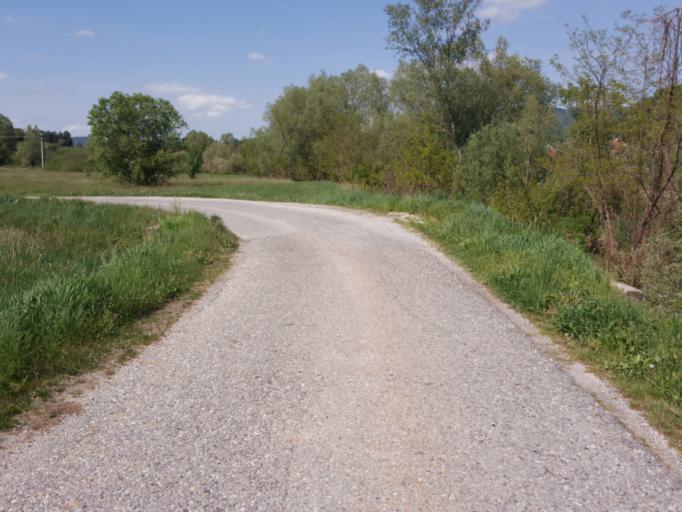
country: HR
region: Varazdinska
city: Lepoglava
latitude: 46.2286
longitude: 15.9654
